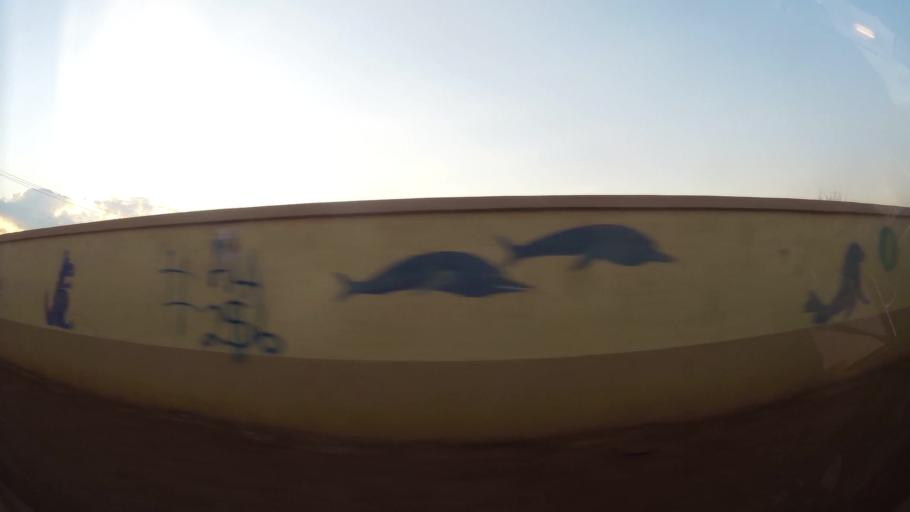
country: ZA
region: Gauteng
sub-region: City of Johannesburg Metropolitan Municipality
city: Orange Farm
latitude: -26.5536
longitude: 27.8689
